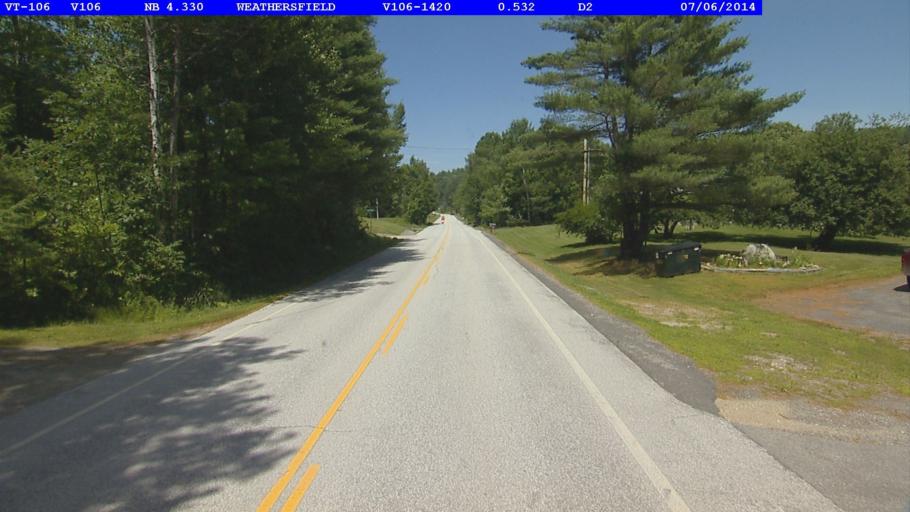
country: US
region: Vermont
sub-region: Windsor County
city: Springfield
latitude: 43.3509
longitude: -72.5252
